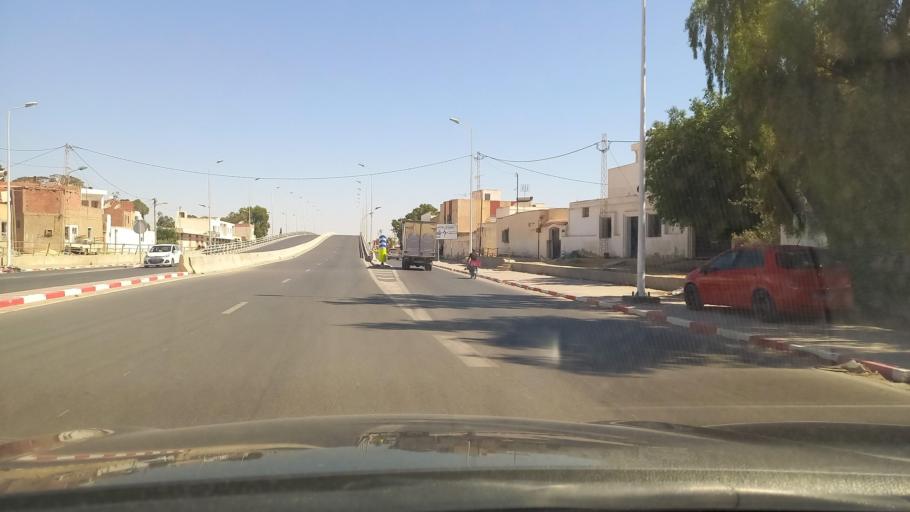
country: TN
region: Safaqis
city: Sfax
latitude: 34.7310
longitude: 10.7251
